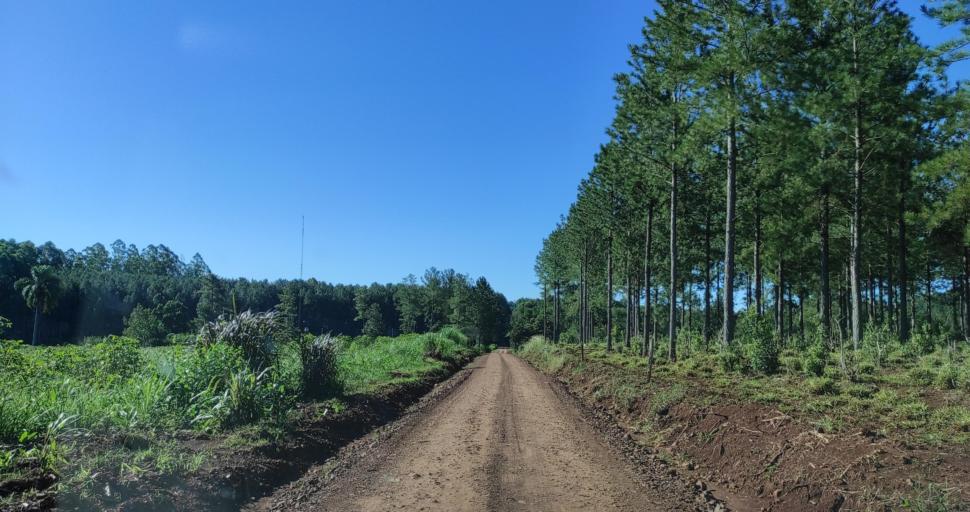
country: AR
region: Misiones
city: Capiovi
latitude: -26.9242
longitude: -55.0006
